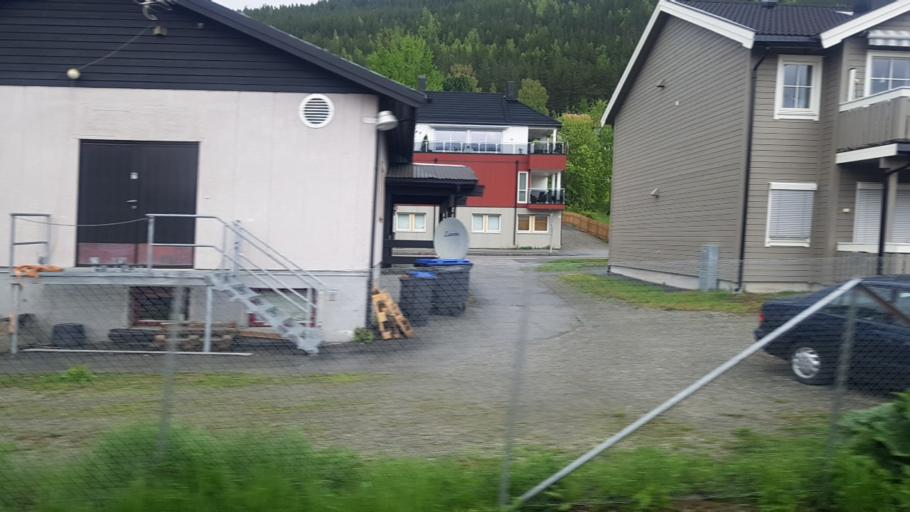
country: NO
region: Oppland
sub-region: Nord-Fron
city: Vinstra
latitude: 61.5941
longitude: 9.7405
